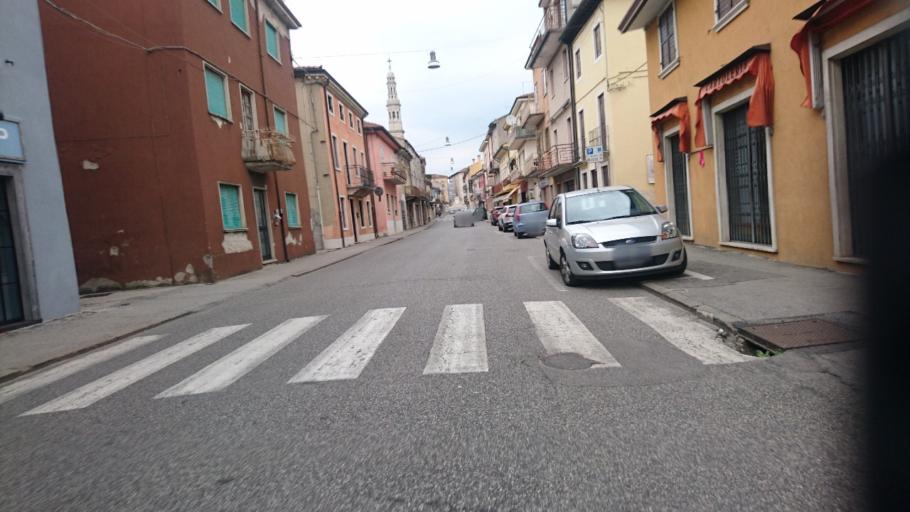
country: IT
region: Veneto
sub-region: Provincia di Verona
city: Monteforte d'Alpone
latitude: 45.4198
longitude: 11.2853
